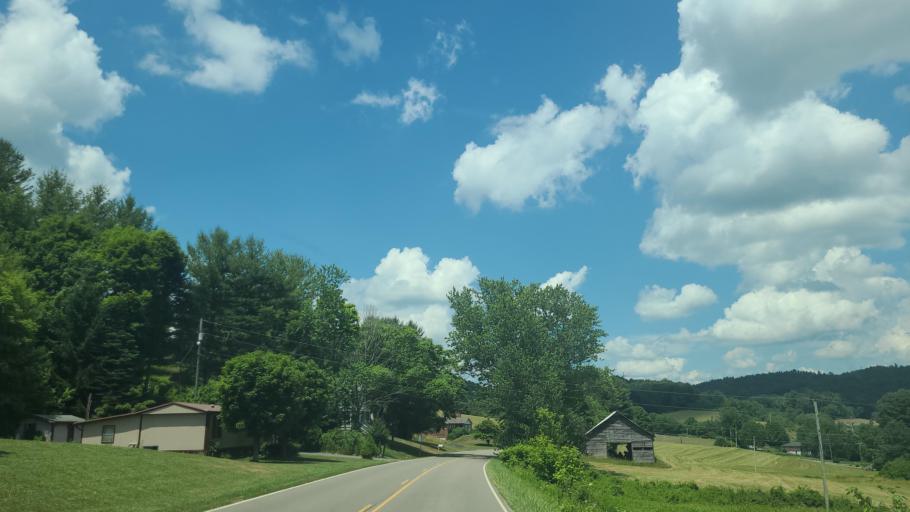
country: US
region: North Carolina
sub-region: Watauga County
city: Boone
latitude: 36.2389
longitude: -81.5444
